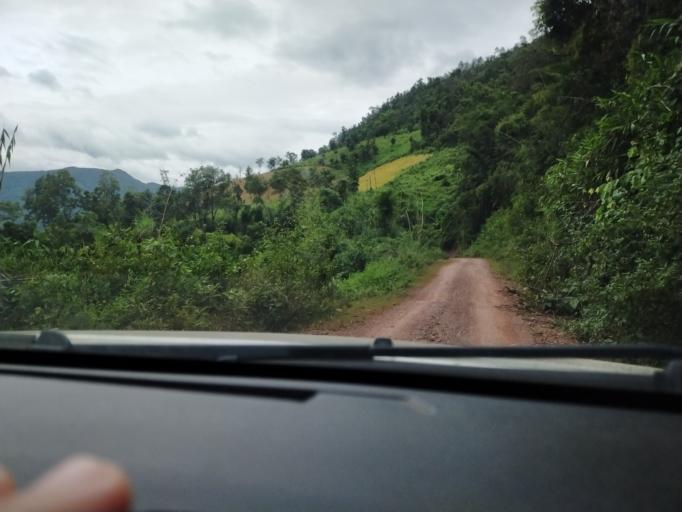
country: TH
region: Nan
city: Chaloem Phra Kiat
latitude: 19.7876
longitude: 101.3606
